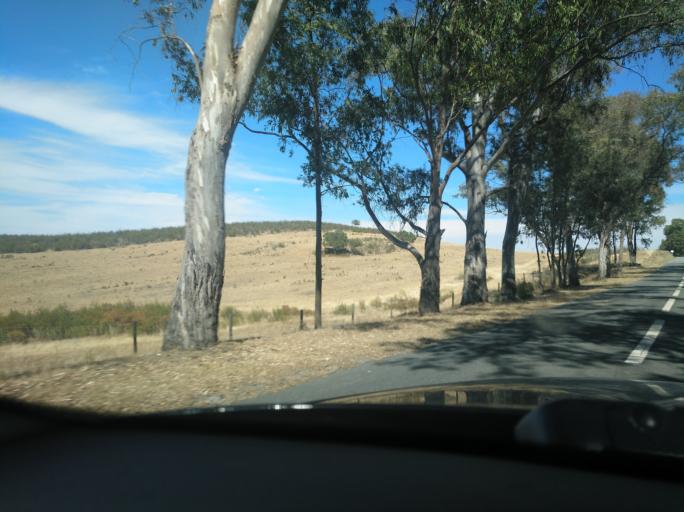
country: PT
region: Beja
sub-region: Mertola
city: Mertola
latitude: 37.6180
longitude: -7.7712
